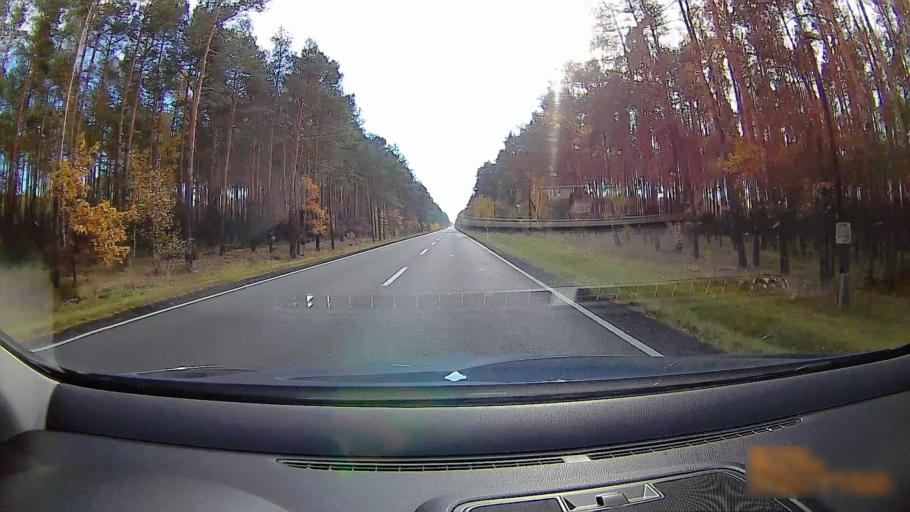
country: PL
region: Greater Poland Voivodeship
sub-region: Powiat ostrzeszowski
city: Ostrzeszow
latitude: 51.4719
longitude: 17.8919
